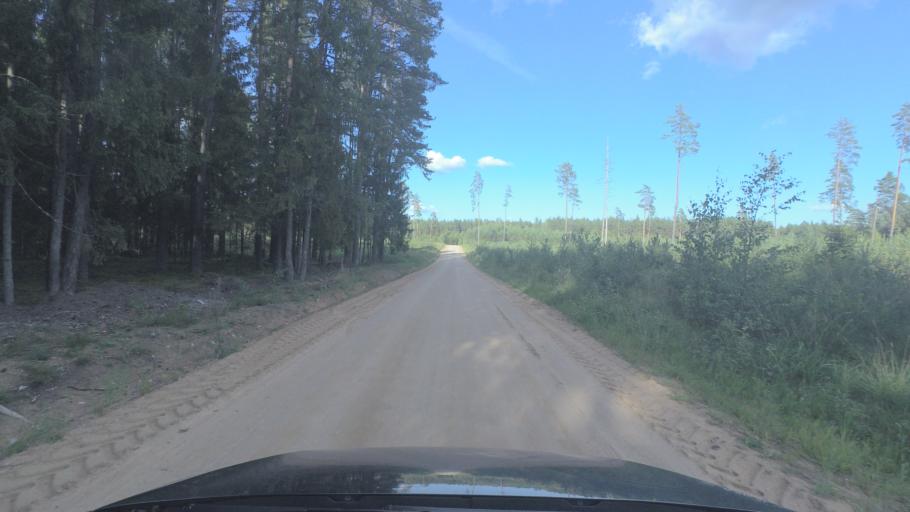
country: LT
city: Pabrade
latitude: 55.1539
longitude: 25.7856
